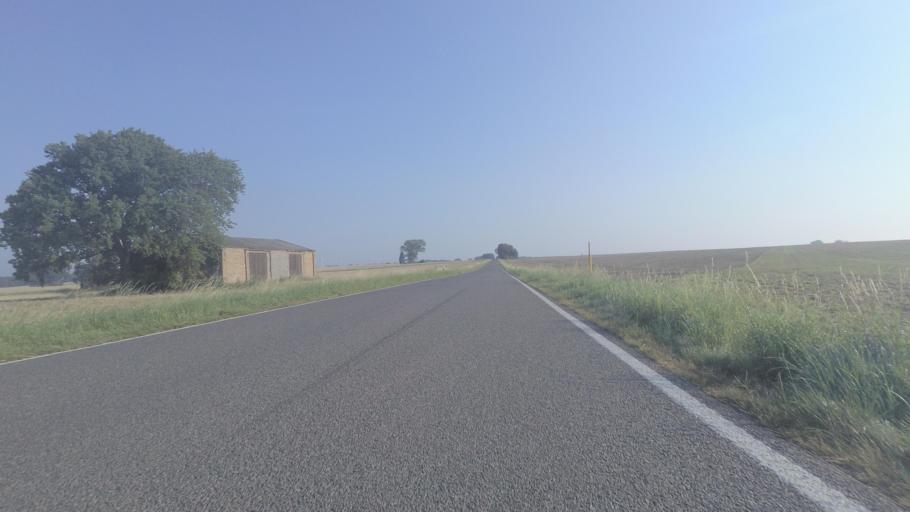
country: DE
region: Brandenburg
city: Heiligengrabe
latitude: 53.2710
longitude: 12.3398
